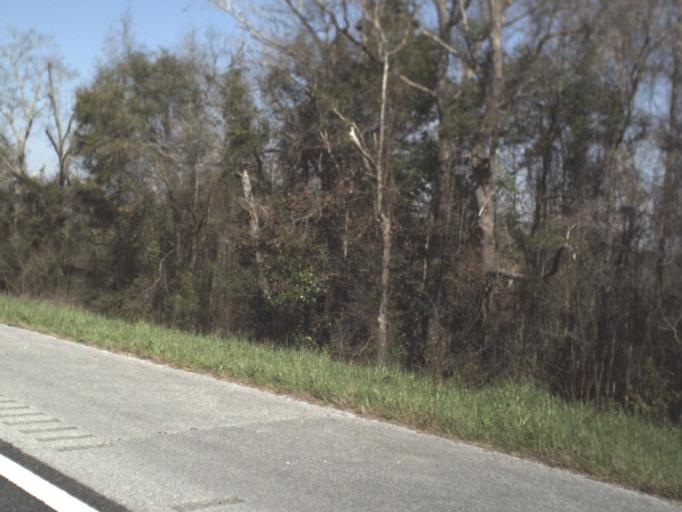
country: US
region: Florida
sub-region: Jackson County
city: Sneads
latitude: 30.6506
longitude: -85.0163
